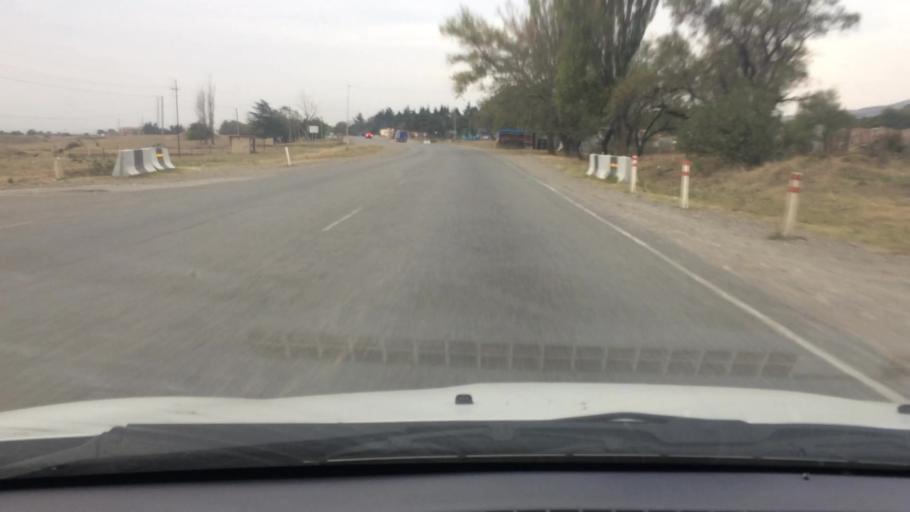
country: GE
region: T'bilisi
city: Tbilisi
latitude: 41.6312
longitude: 44.8120
